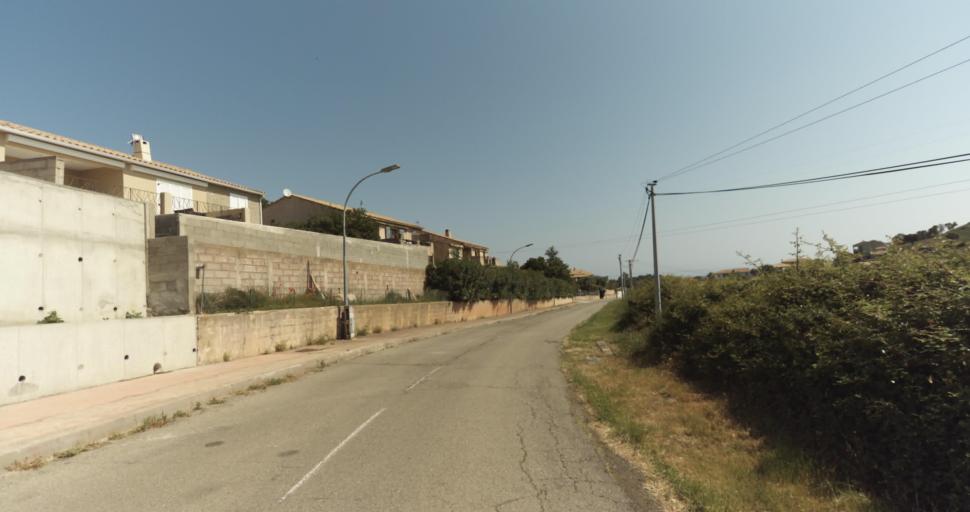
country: FR
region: Corsica
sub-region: Departement de la Haute-Corse
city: Biguglia
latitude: 42.6176
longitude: 9.4233
